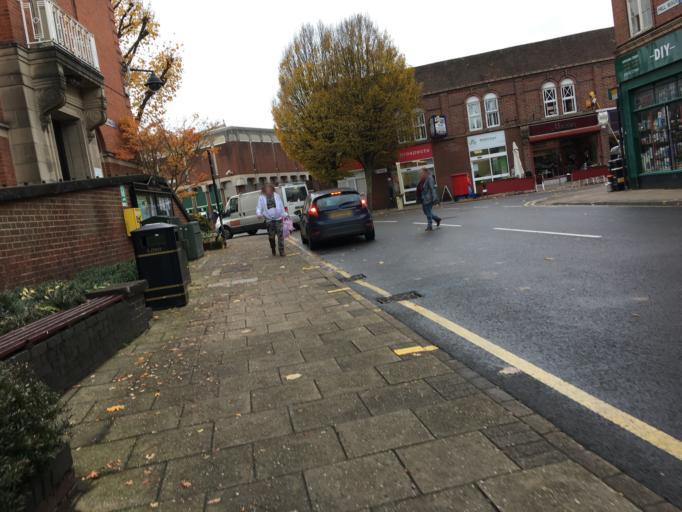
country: GB
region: England
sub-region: Warwickshire
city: Nuneaton
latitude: 52.5222
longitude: -1.4673
